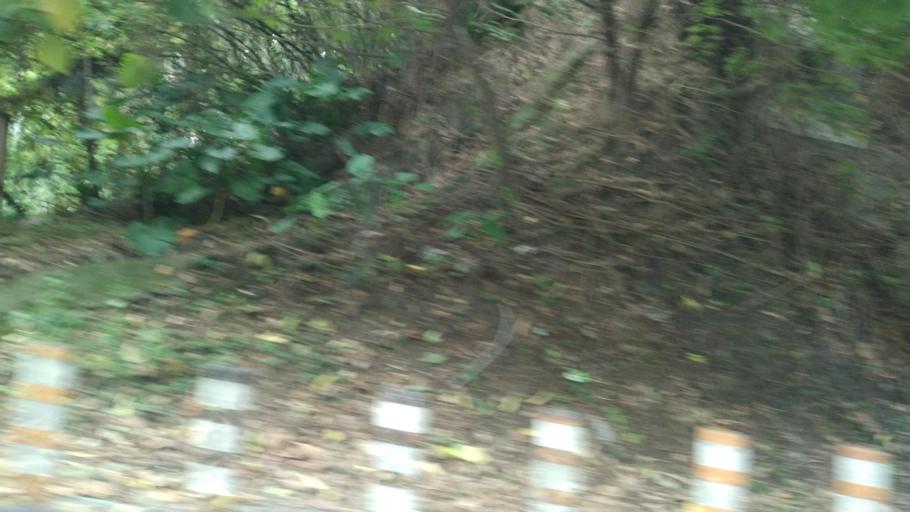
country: TW
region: Taiwan
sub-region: Taoyuan
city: Taoyuan
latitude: 24.9594
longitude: 121.3705
